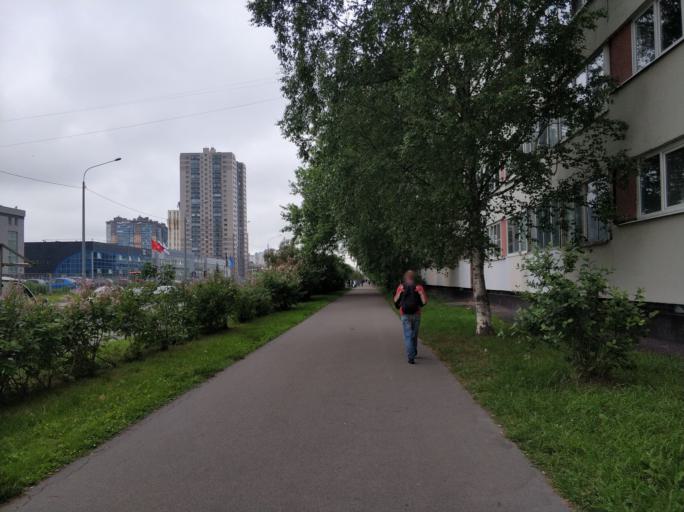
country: RU
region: St.-Petersburg
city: Grazhdanka
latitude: 60.0332
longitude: 30.4083
